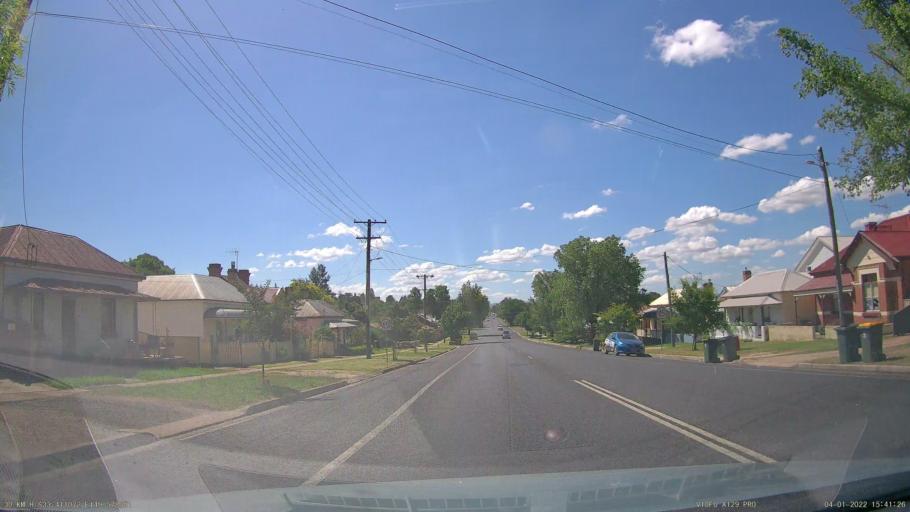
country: AU
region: New South Wales
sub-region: Bathurst Regional
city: Bathurst
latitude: -33.4109
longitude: 149.5786
